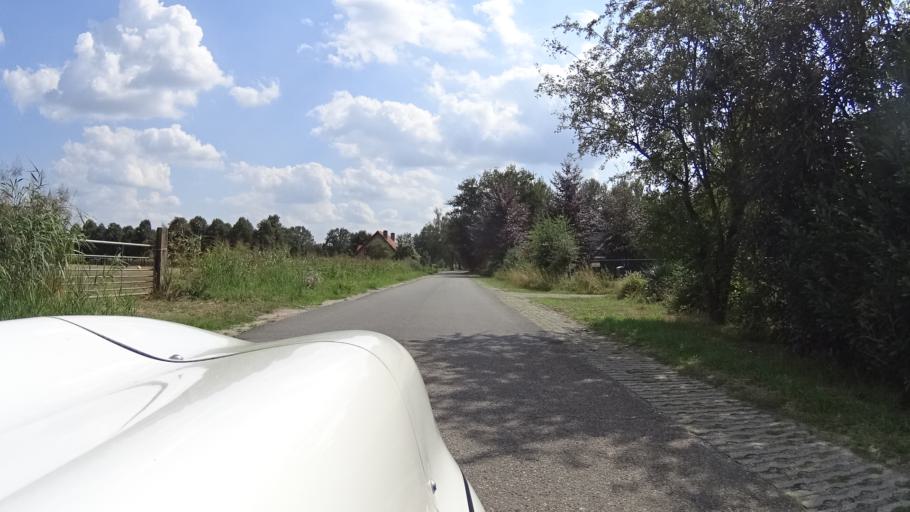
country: NL
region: North Brabant
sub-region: Gemeente Veghel
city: Mariaheide
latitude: 51.6502
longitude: 5.5564
